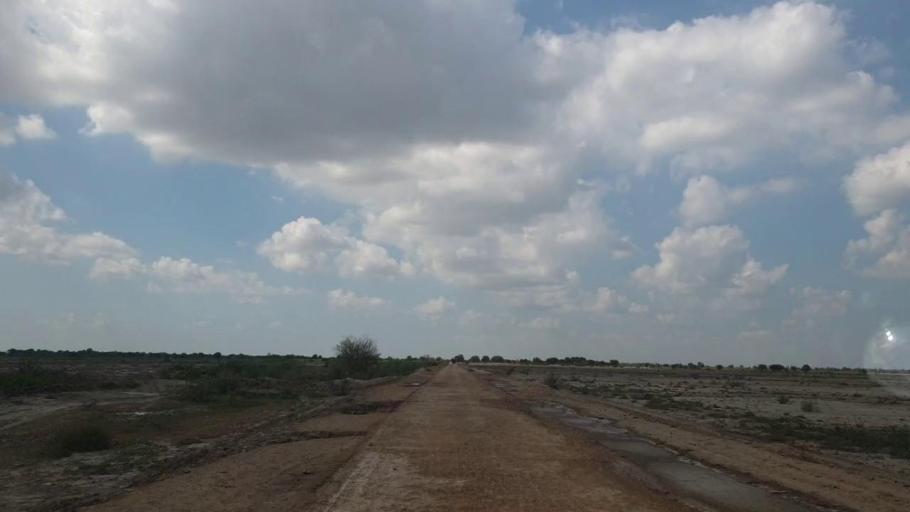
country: PK
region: Sindh
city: Pithoro
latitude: 25.5992
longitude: 69.3590
